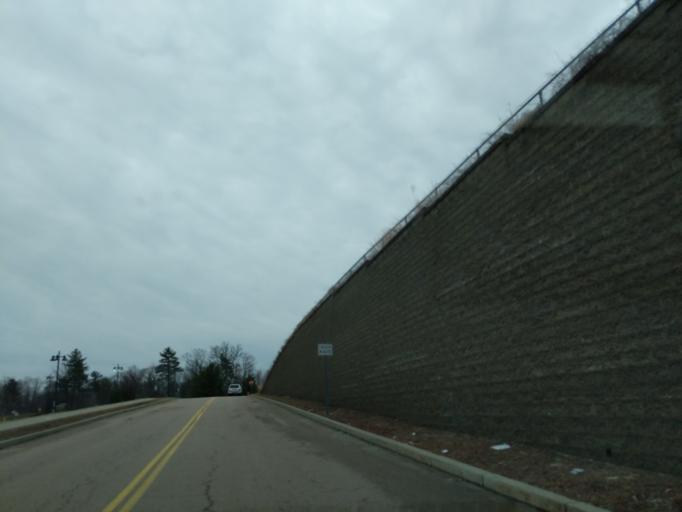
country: US
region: Massachusetts
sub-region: Worcester County
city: Whitinsville
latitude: 42.1067
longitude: -71.7013
